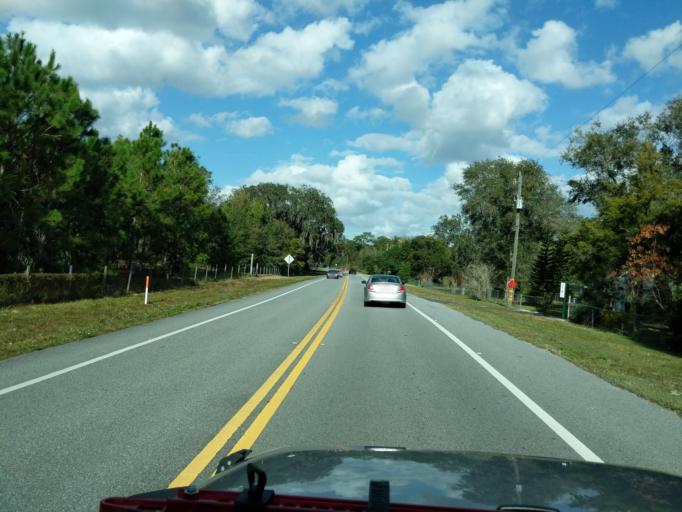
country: US
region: Florida
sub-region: Seminole County
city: Geneva
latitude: 28.7145
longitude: -81.1185
